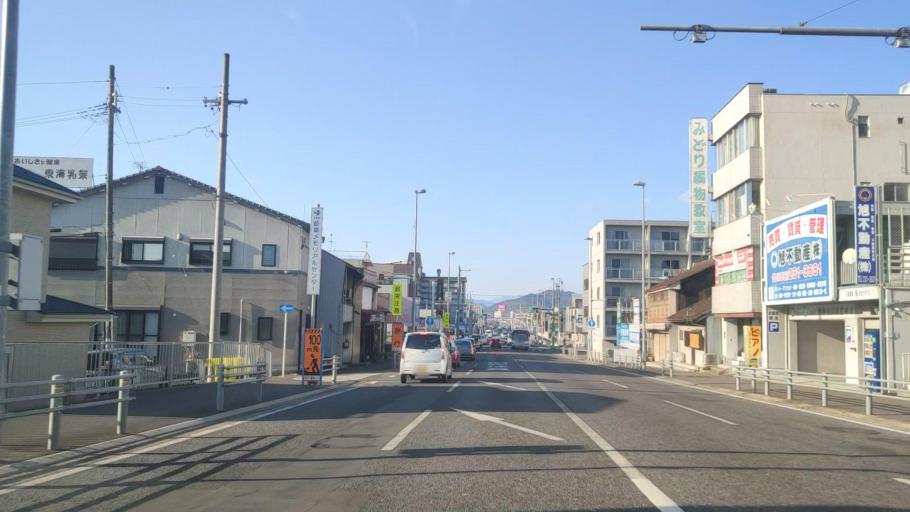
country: JP
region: Gifu
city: Gifu-shi
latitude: 35.4331
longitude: 136.7494
